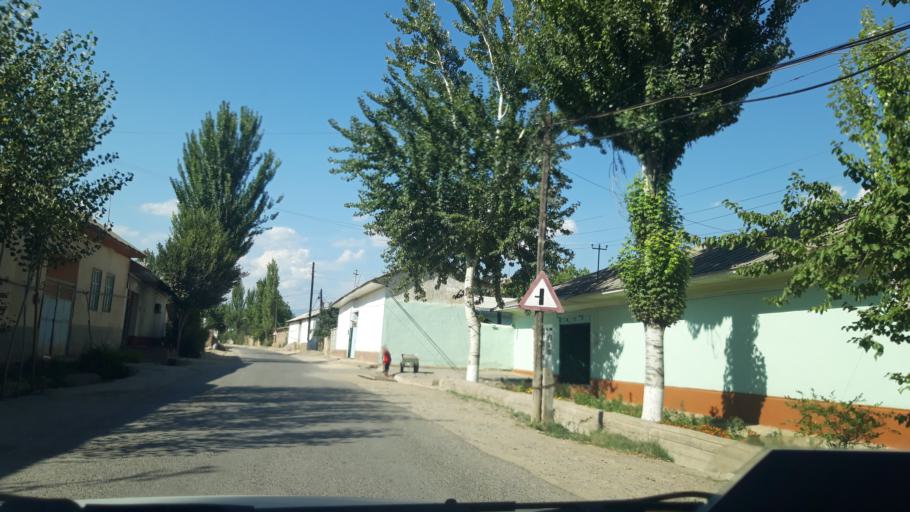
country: UZ
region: Namangan
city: Yangiqo`rg`on
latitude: 41.2035
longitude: 71.7259
